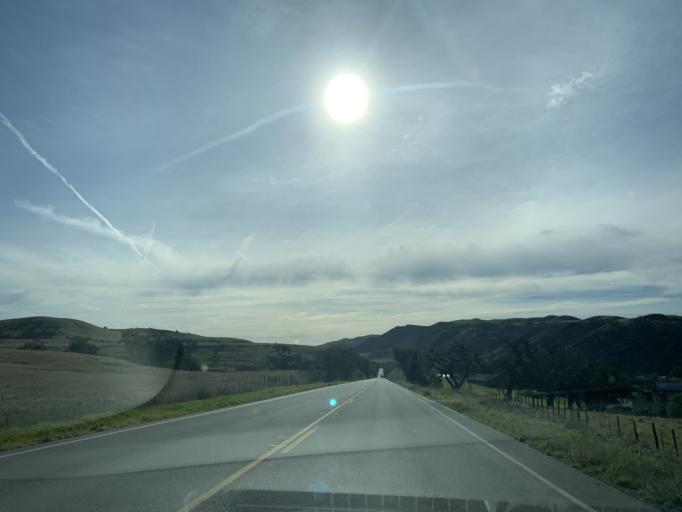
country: US
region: California
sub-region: San Benito County
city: Ridgemark
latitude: 36.7849
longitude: -121.3148
